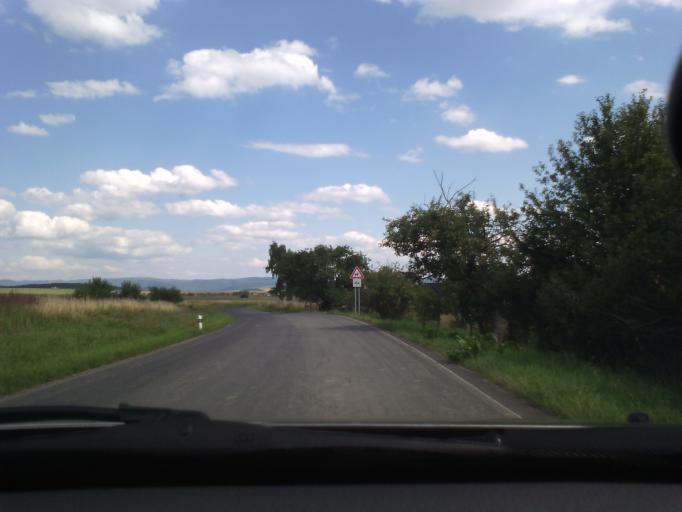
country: SK
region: Presovsky
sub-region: Okres Poprad
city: Nova Lesna
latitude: 49.1327
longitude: 20.3148
